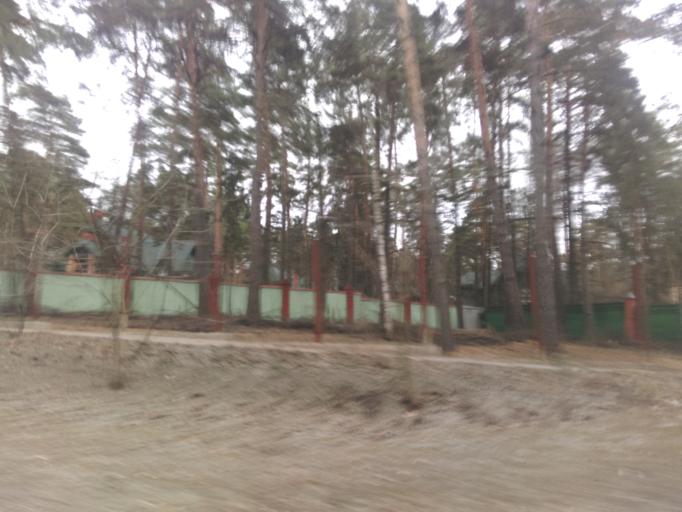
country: RU
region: Moskovskaya
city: Barvikha
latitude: 55.7439
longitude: 37.2830
